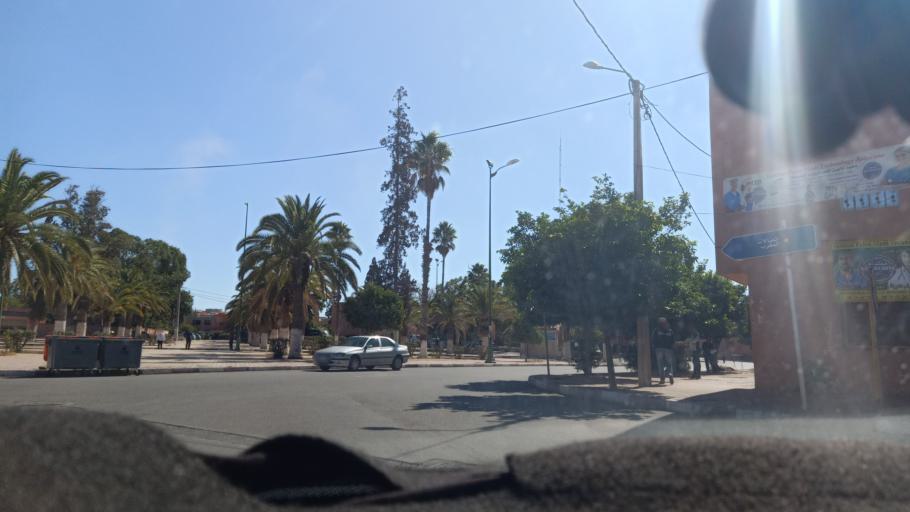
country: MA
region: Doukkala-Abda
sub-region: Safi
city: Youssoufia
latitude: 32.2452
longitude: -8.5332
